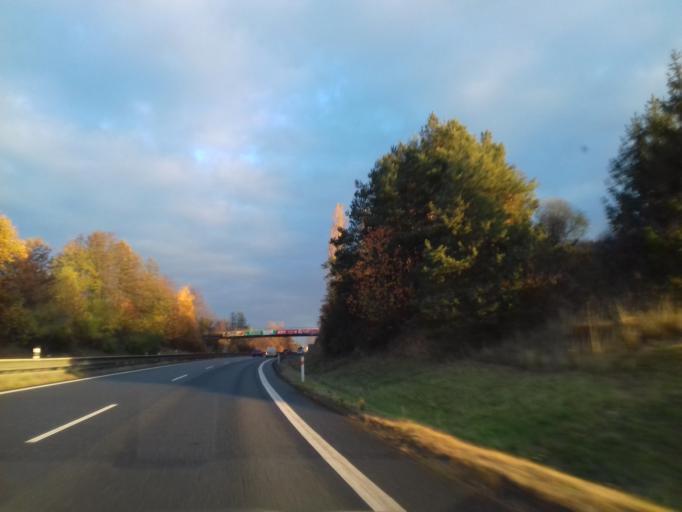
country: CZ
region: Olomoucky
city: Urcice
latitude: 49.4350
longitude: 17.1087
